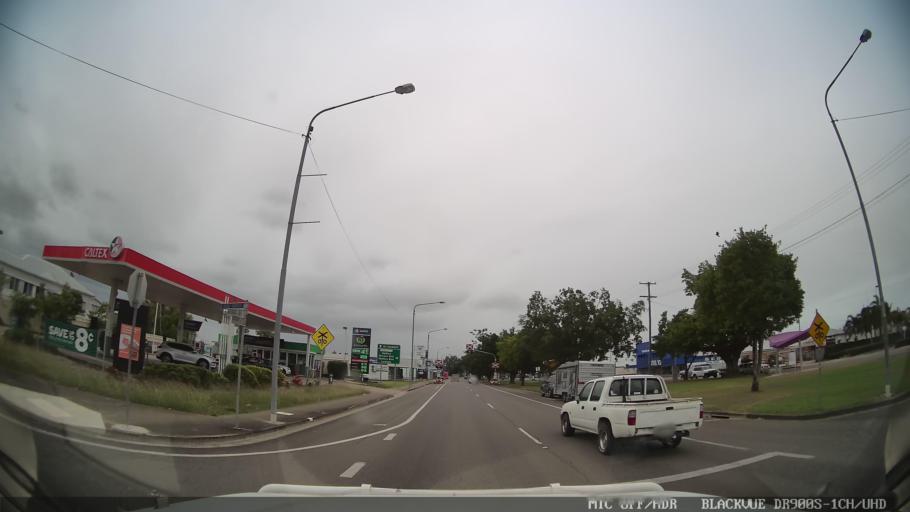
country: AU
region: Queensland
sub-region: Hinchinbrook
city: Ingham
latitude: -18.6476
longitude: 146.1602
